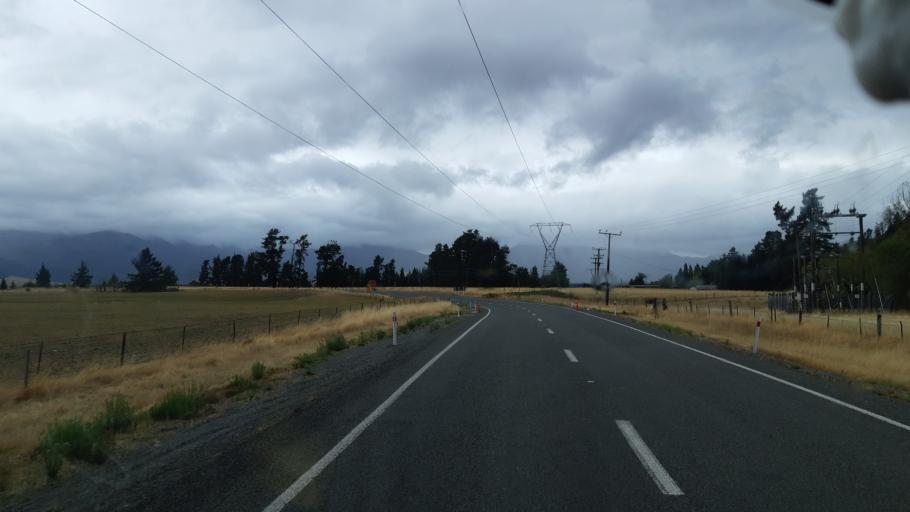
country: NZ
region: Canterbury
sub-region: Hurunui District
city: Amberley
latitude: -42.5874
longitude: 172.7773
